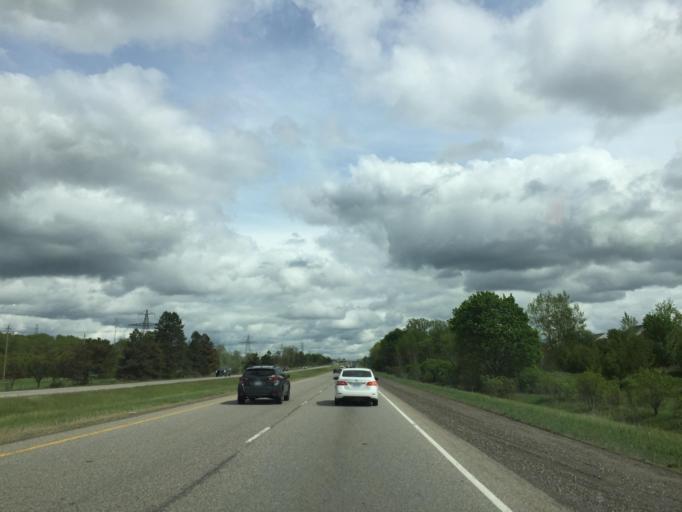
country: CA
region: Ontario
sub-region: Wellington County
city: Guelph
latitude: 43.5024
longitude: -80.2295
